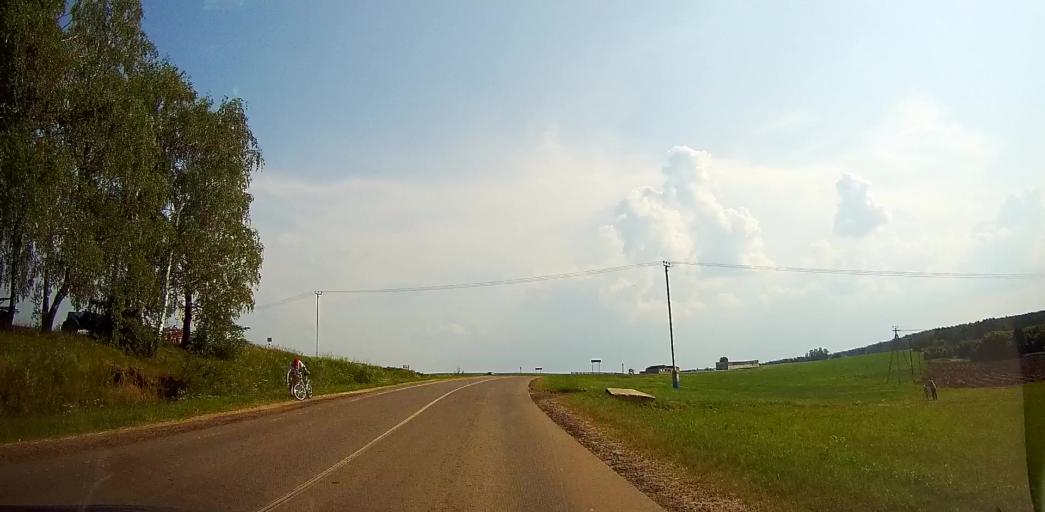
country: RU
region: Moskovskaya
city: Il'inskoye
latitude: 55.2922
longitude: 37.9430
